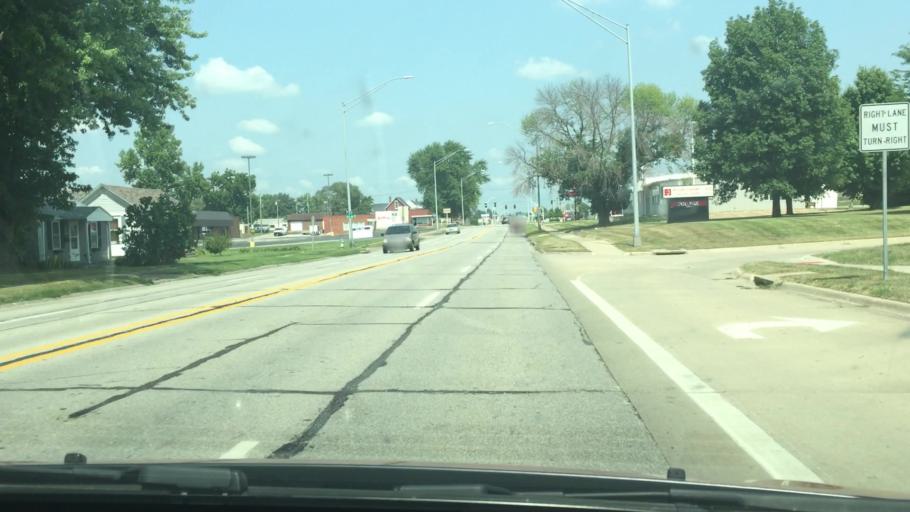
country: US
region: Iowa
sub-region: Muscatine County
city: Muscatine
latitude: 41.4396
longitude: -91.0306
